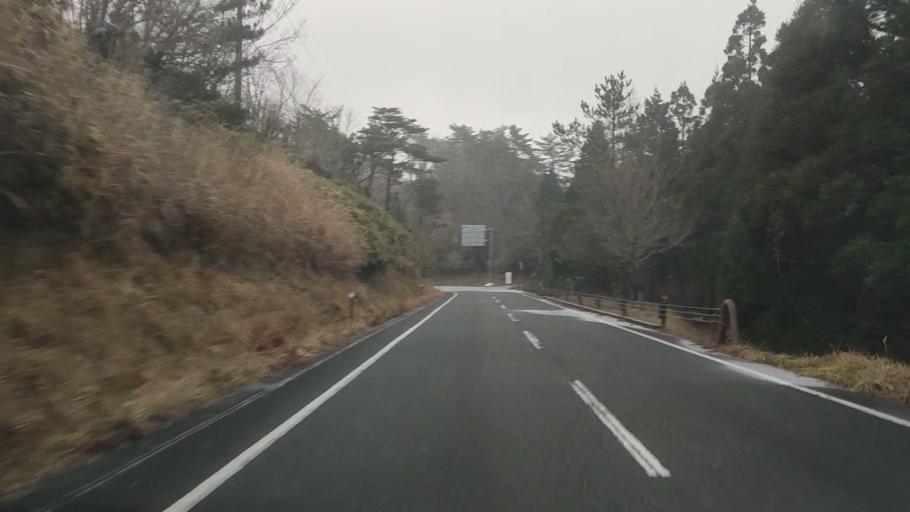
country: JP
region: Kumamoto
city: Matsubase
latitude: 32.5707
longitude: 130.9077
